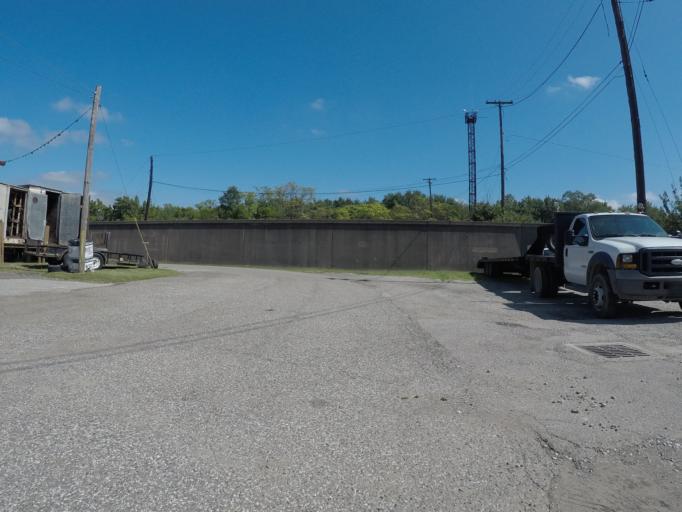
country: US
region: Kentucky
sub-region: Boyd County
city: Ashland
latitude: 38.4692
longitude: -82.6191
